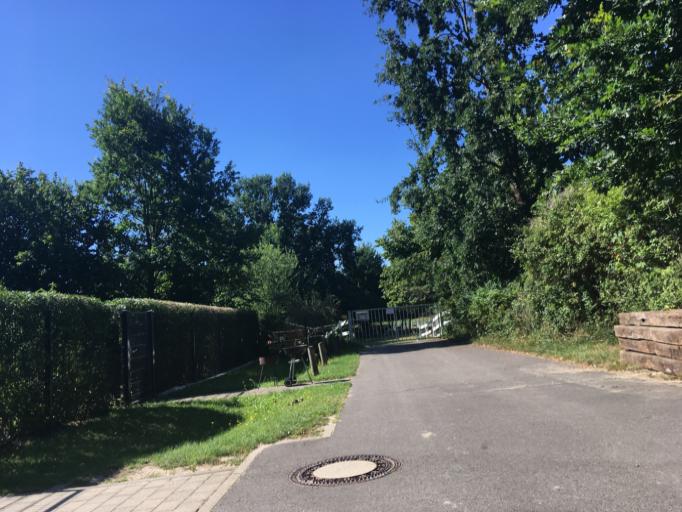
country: DE
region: Brandenburg
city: Altlandsberg
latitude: 52.5464
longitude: 13.7205
